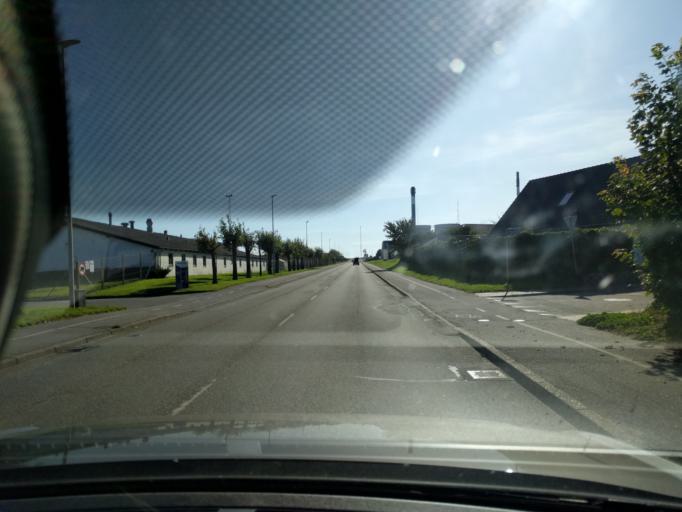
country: DK
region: North Denmark
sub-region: Vesthimmerland Kommune
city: Logstor
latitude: 56.9613
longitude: 9.2653
